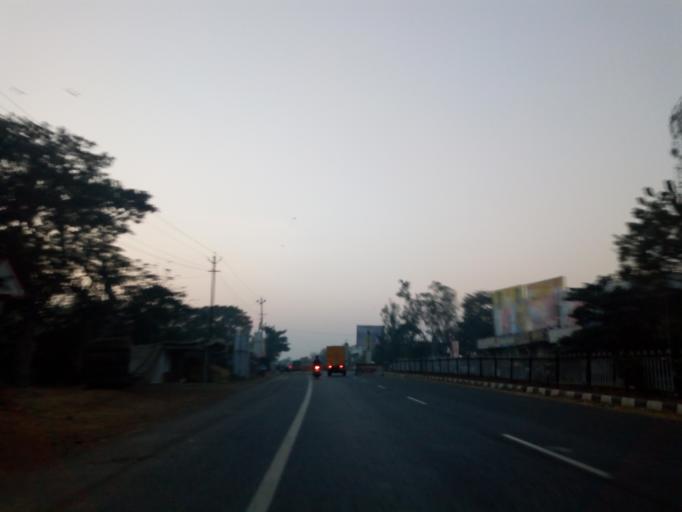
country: IN
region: Andhra Pradesh
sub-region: West Godavari
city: Tadepallegudem
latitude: 16.8235
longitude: 81.4233
